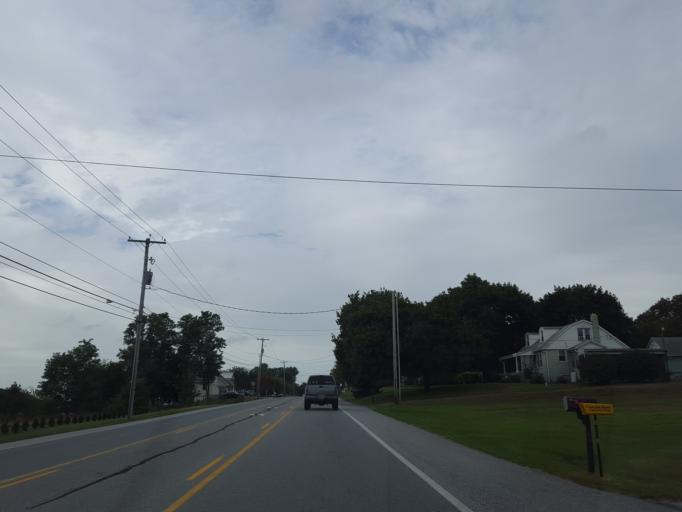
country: US
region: Pennsylvania
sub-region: Adams County
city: Abbottstown
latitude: 39.8993
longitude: -76.9508
